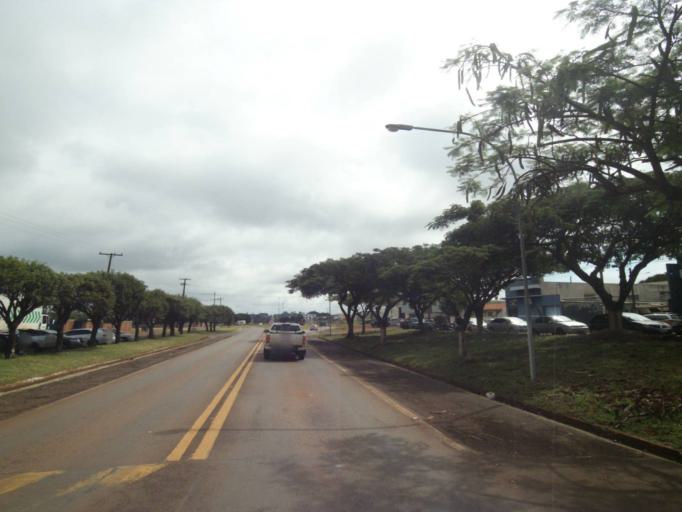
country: BR
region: Parana
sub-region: Campo Mourao
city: Campo Mourao
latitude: -24.0218
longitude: -52.3640
